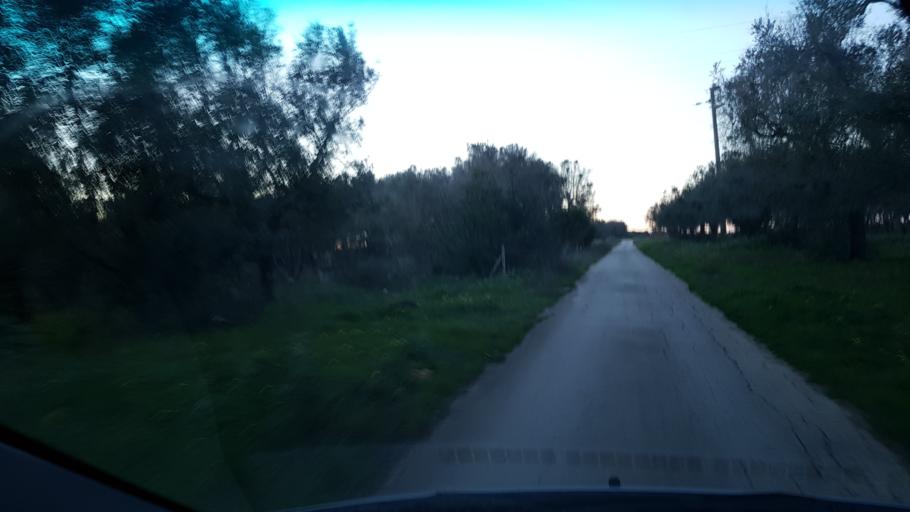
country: IT
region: Apulia
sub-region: Provincia di Brindisi
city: San Pietro Vernotico
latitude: 40.5032
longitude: 17.9777
